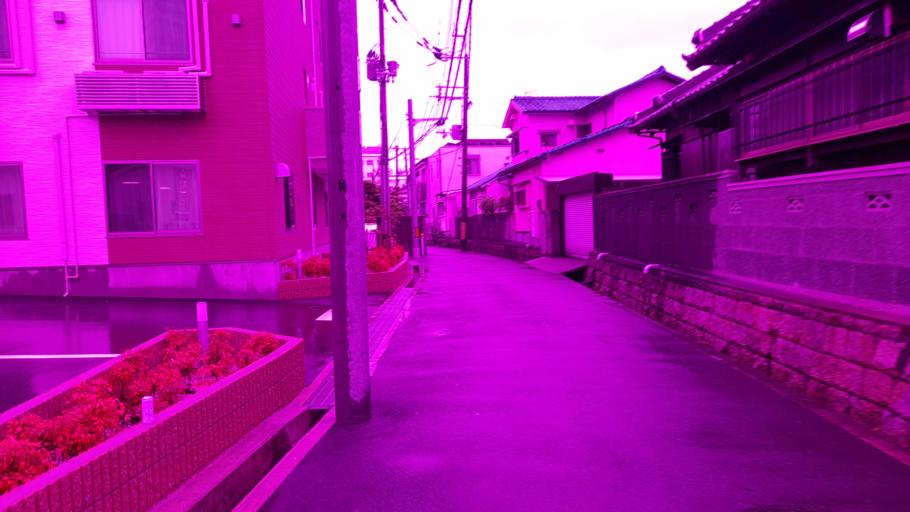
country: JP
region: Osaka
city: Toyonaka
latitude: 34.7642
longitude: 135.4579
